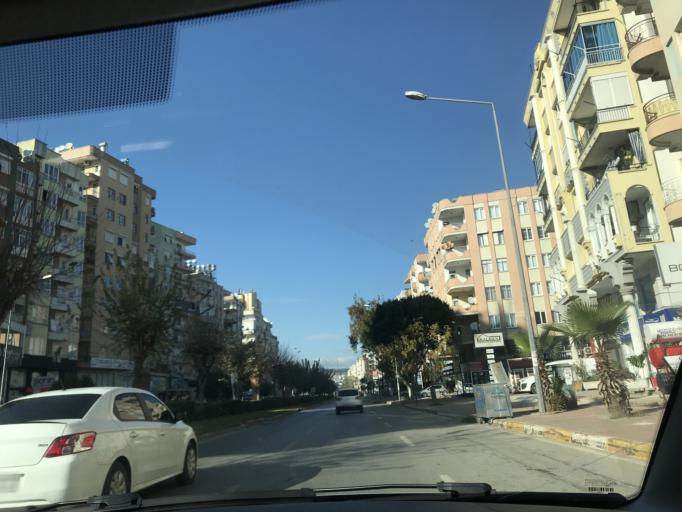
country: TR
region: Antalya
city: Antalya
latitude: 36.9045
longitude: 30.7007
